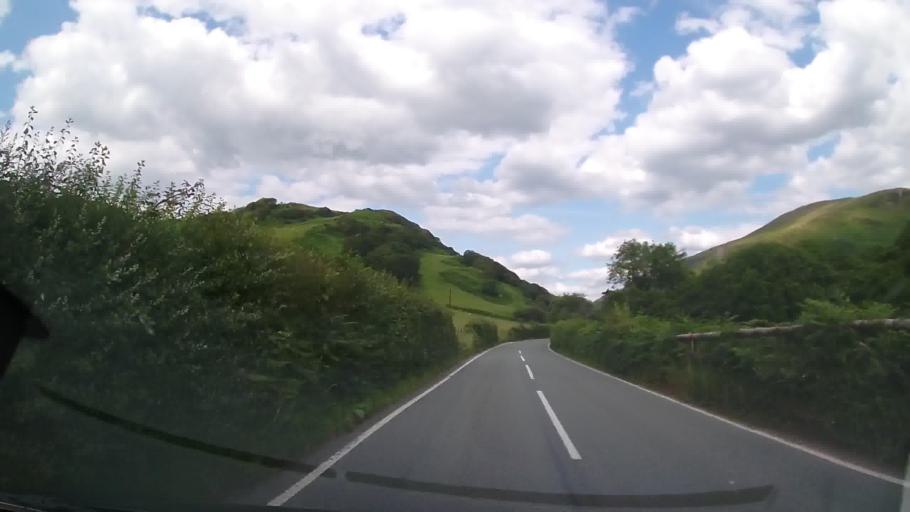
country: GB
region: Wales
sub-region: Gwynedd
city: Tywyn
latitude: 52.6222
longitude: -4.0034
